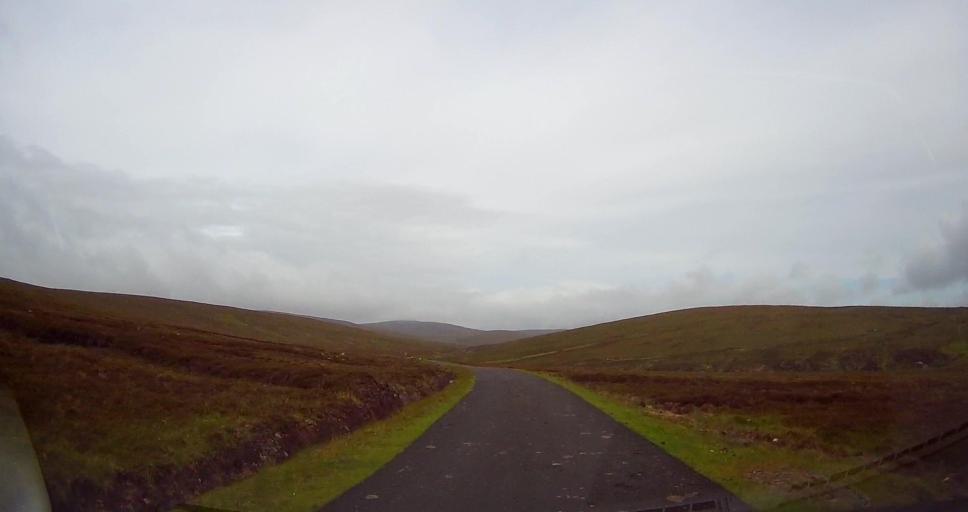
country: GB
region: Scotland
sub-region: Orkney Islands
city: Stromness
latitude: 58.8582
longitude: -3.2178
